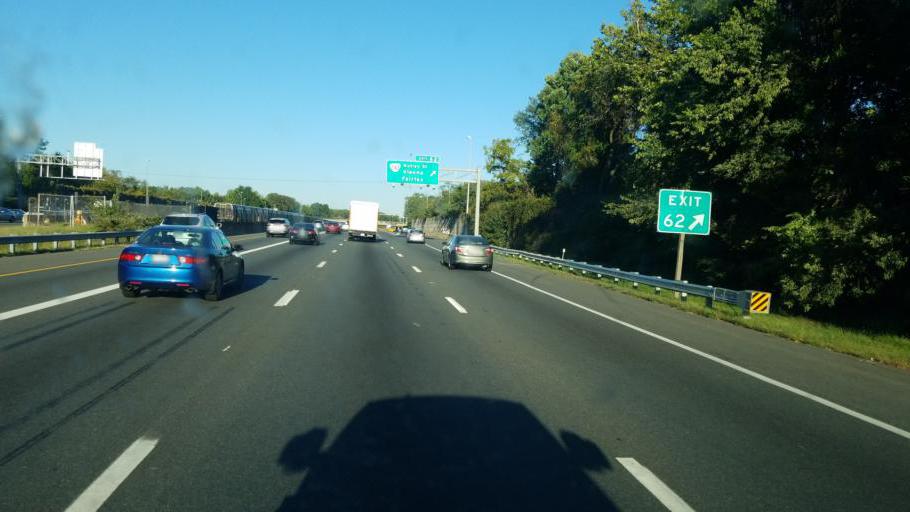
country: US
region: Virginia
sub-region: Fairfax County
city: Oakton
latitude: 38.8753
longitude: -77.2810
